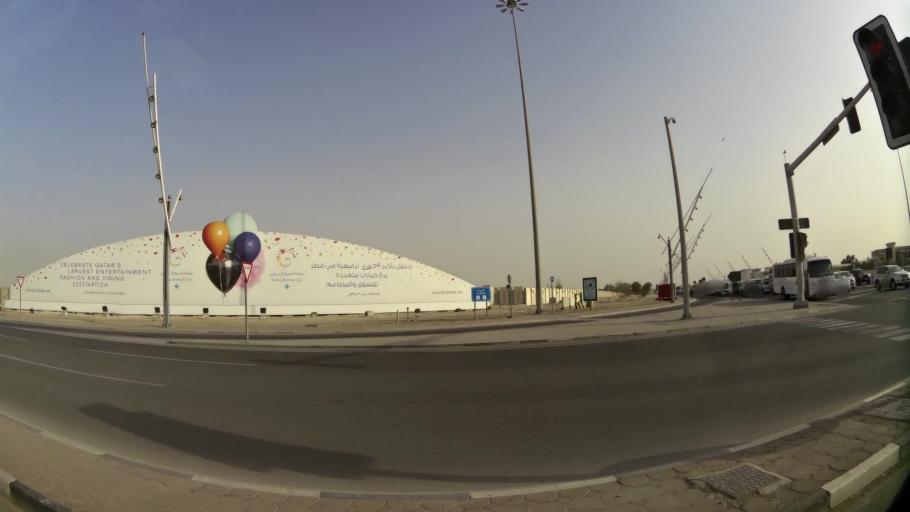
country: QA
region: Baladiyat ar Rayyan
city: Ar Rayyan
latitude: 25.2523
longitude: 51.4314
